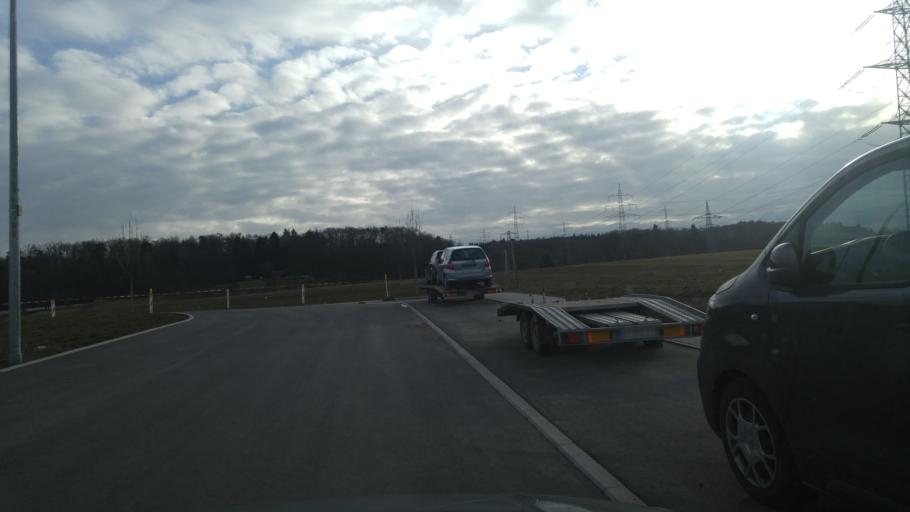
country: DE
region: Baden-Wuerttemberg
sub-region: Regierungsbezirk Stuttgart
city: Leonberg
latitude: 48.7902
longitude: 8.9797
